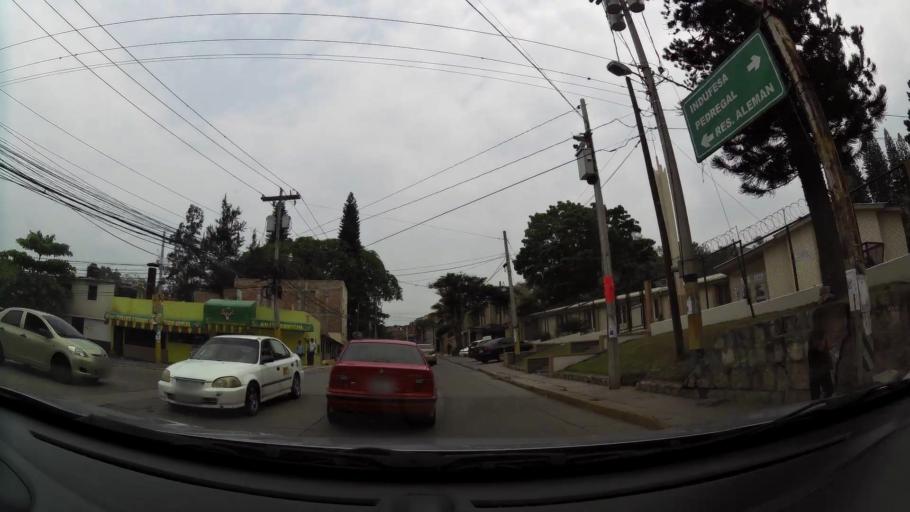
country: HN
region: Francisco Morazan
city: Tegucigalpa
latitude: 14.0620
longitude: -87.2004
